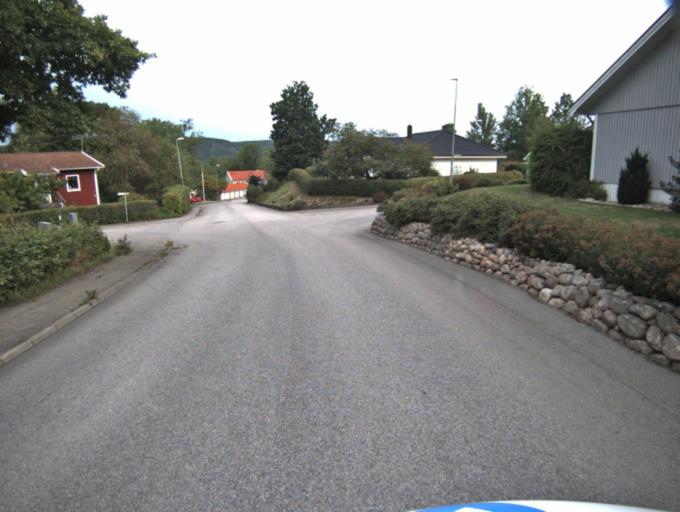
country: SE
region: Vaestra Goetaland
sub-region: Ulricehamns Kommun
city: Ulricehamn
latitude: 57.8024
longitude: 13.4278
